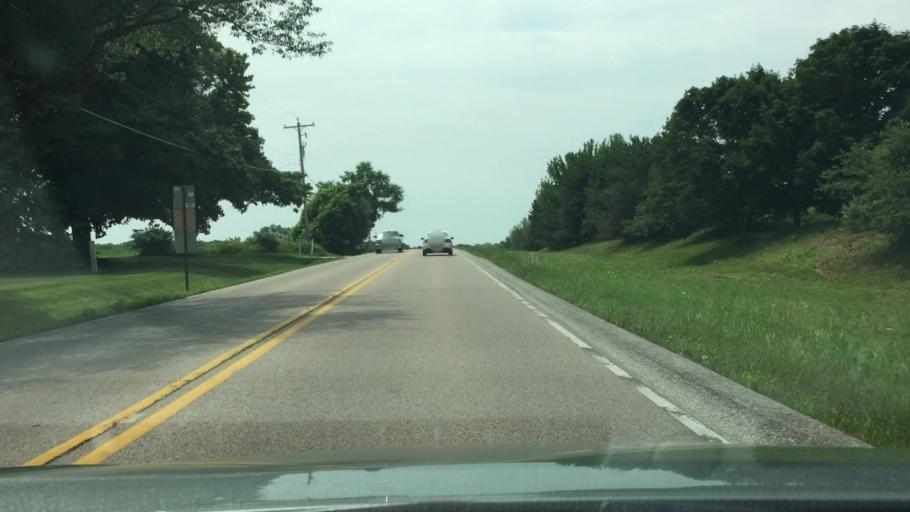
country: US
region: Wisconsin
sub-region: Waukesha County
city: Merton
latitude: 43.1171
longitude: -88.3131
